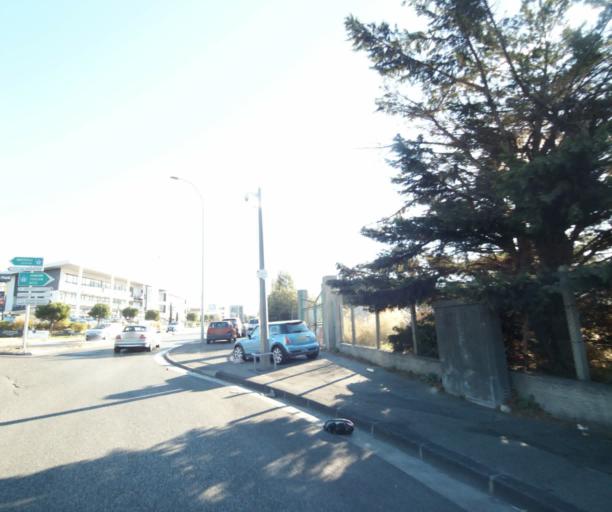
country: FR
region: Provence-Alpes-Cote d'Azur
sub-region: Departement des Bouches-du-Rhone
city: Marseille 11
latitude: 43.2899
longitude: 5.4765
